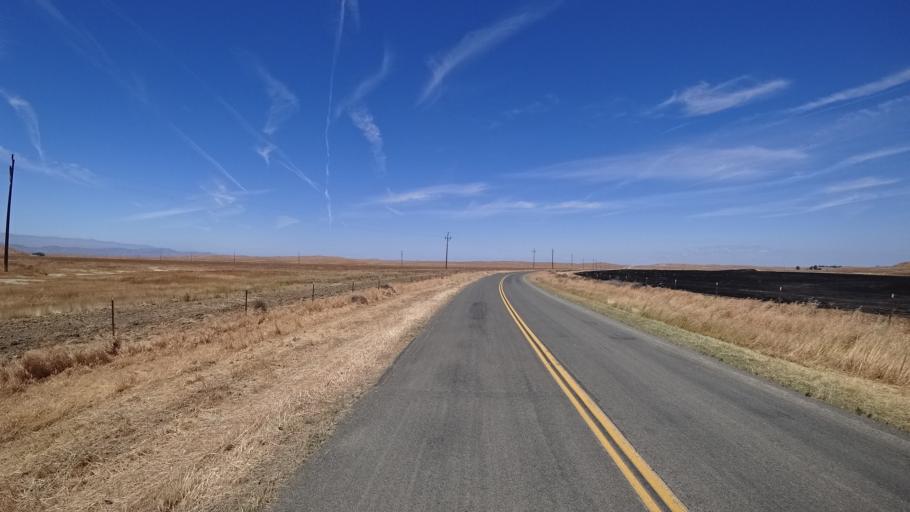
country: US
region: California
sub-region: Kings County
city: Kettleman City
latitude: 35.8330
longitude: -119.9148
